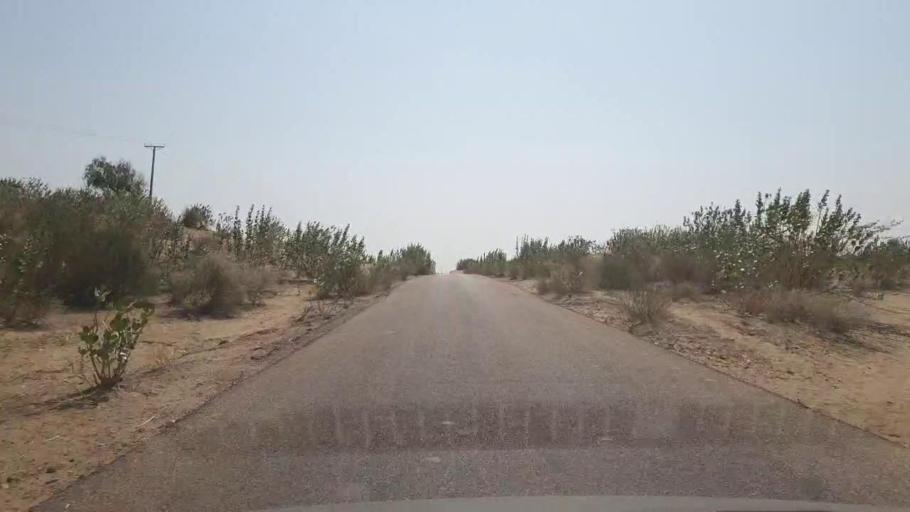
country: PK
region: Sindh
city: Chor
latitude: 25.6484
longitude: 70.1689
